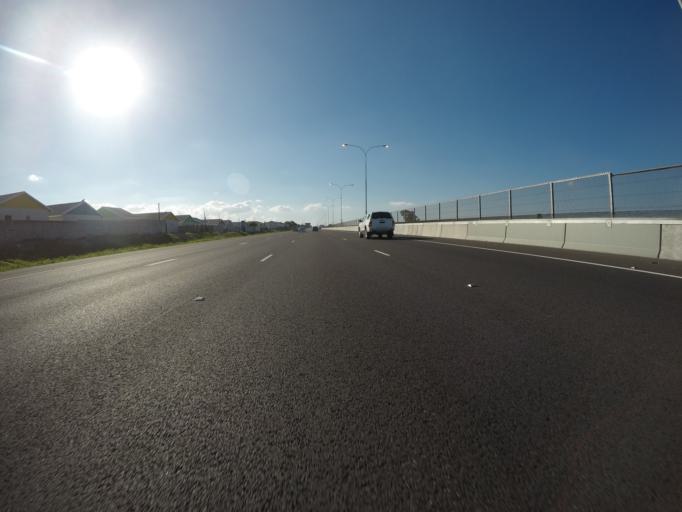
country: ZA
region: Western Cape
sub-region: City of Cape Town
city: Kraaifontein
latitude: -33.9633
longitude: 18.6555
